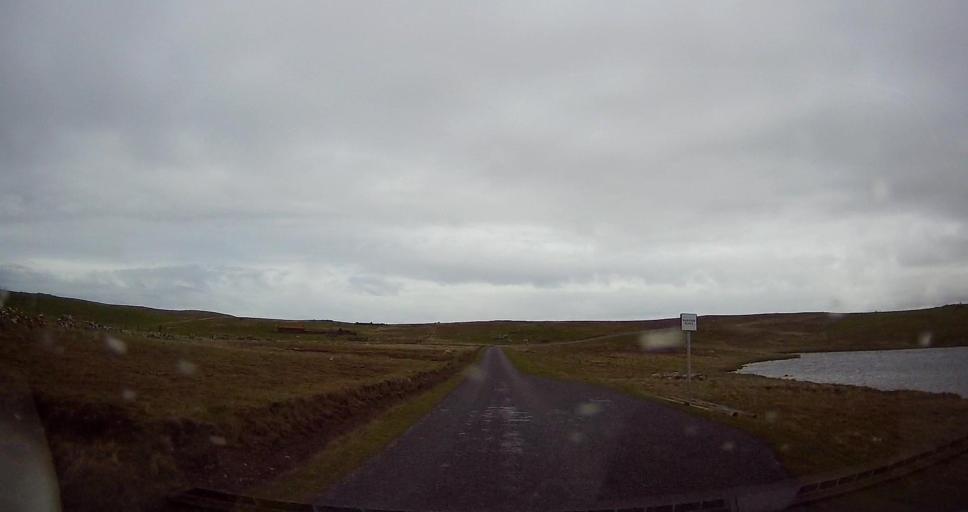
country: GB
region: Scotland
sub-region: Shetland Islands
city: Lerwick
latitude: 60.4836
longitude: -1.6078
